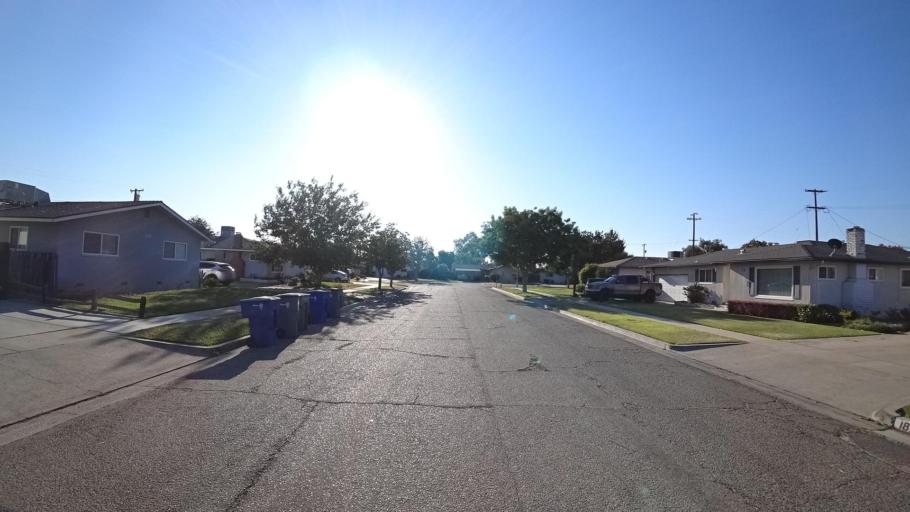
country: US
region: California
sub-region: Fresno County
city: Fresno
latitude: 36.7767
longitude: -119.8326
